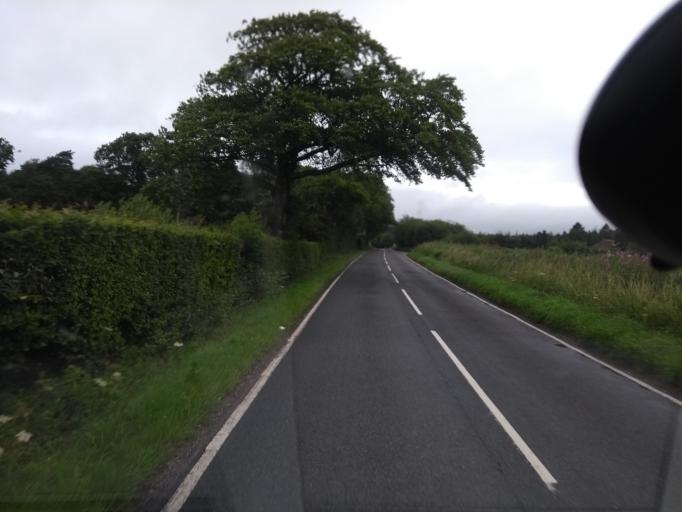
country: GB
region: England
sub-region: Somerset
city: Taunton
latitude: 50.9382
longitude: -3.0996
